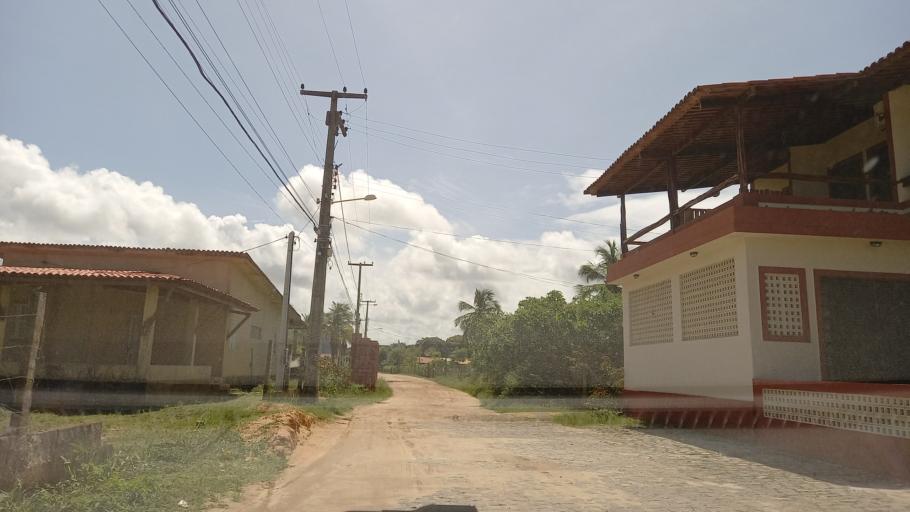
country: BR
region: Pernambuco
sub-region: Sao Jose Da Coroa Grande
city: Sao Jose da Coroa Grande
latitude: -8.9246
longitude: -35.1610
